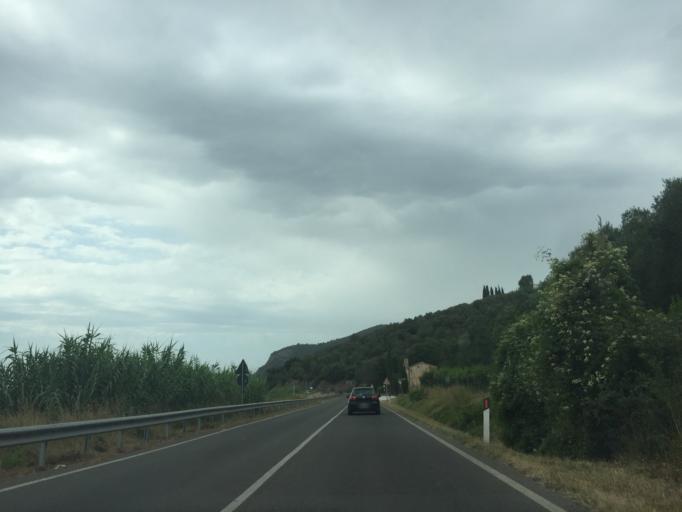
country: IT
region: Tuscany
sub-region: Province of Pisa
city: Asciano
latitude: 43.7397
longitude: 10.4723
